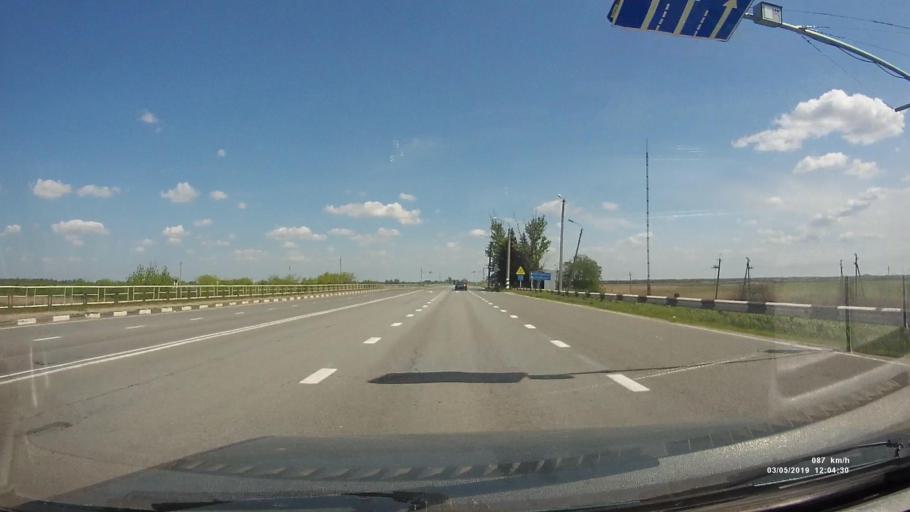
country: RU
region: Rostov
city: Bagayevskaya
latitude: 47.2788
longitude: 40.4117
